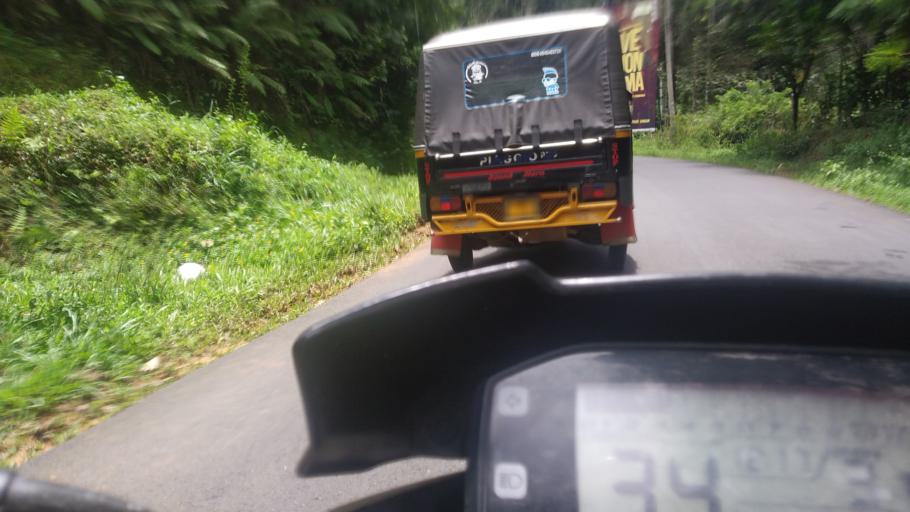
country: IN
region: Kerala
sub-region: Idukki
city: Munnar
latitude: 10.0175
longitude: 77.0087
